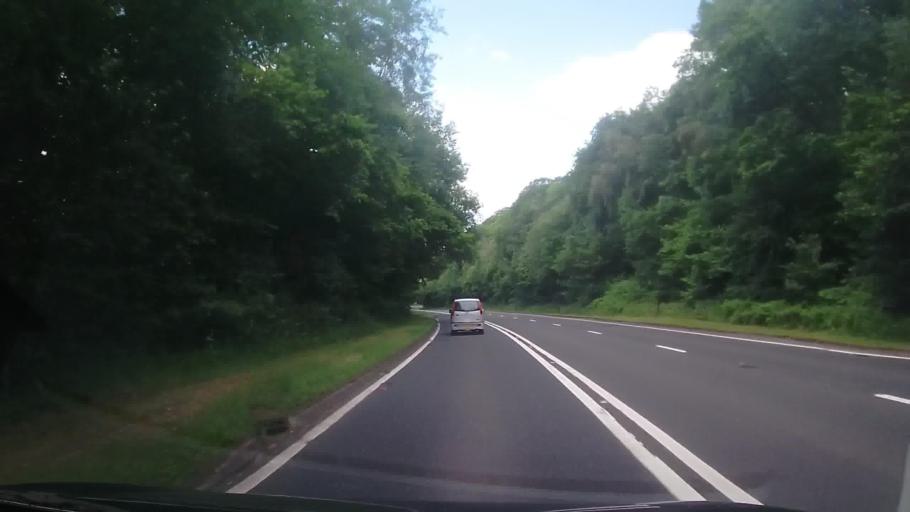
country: GB
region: England
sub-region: Herefordshire
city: Hope under Dinmore
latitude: 52.1678
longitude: -2.7191
